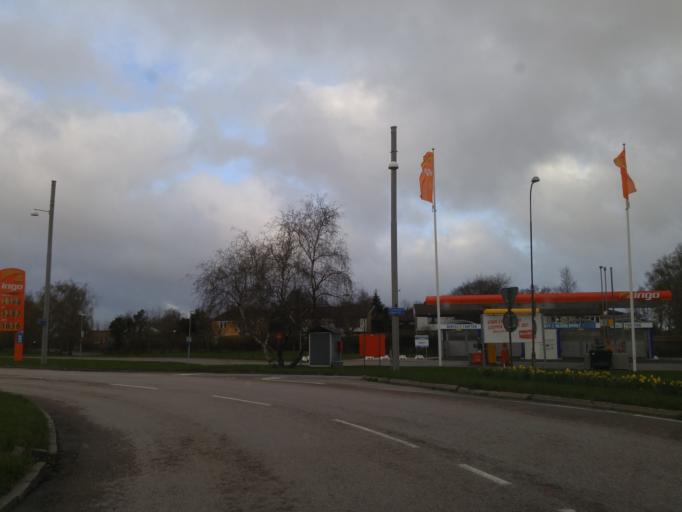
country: SE
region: Vaestra Goetaland
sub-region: Goteborg
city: Majorna
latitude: 57.6603
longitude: 11.8894
